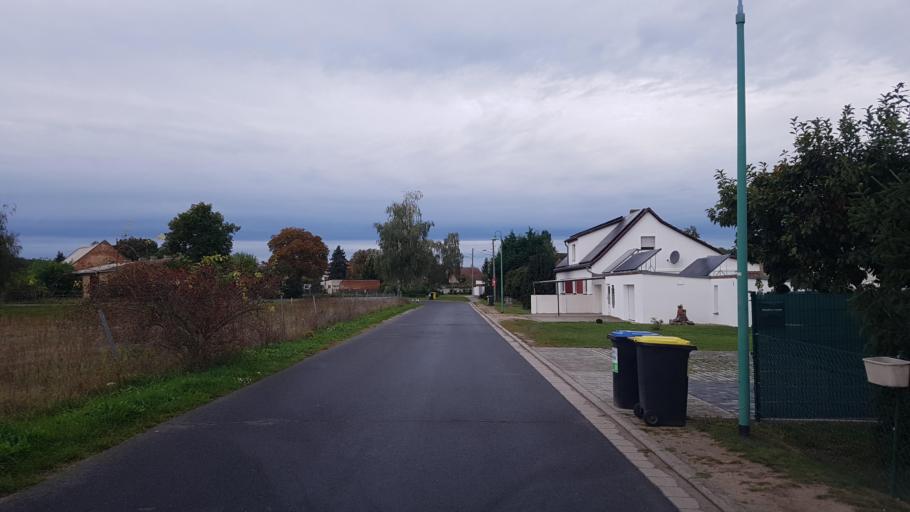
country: DE
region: Brandenburg
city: Golssen
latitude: 51.9481
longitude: 13.6476
